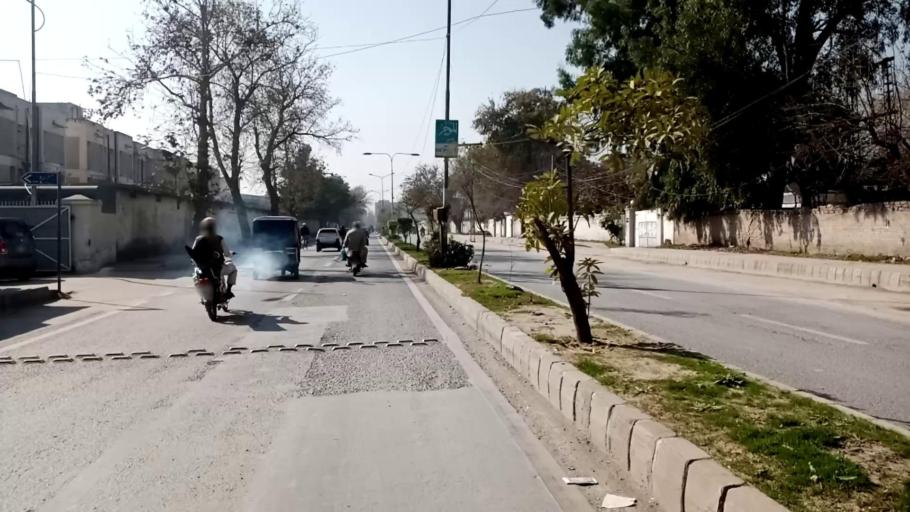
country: PK
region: Khyber Pakhtunkhwa
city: Peshawar
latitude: 33.9877
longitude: 71.5313
